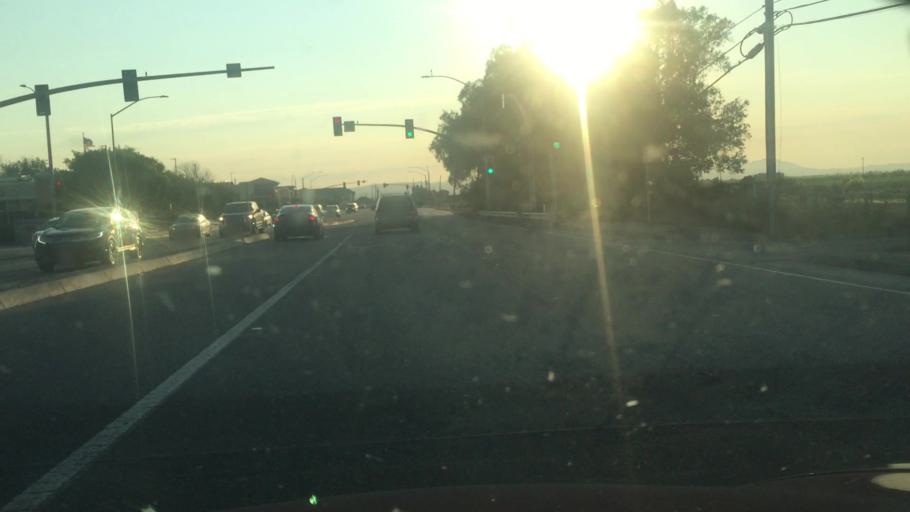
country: US
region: California
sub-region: San Joaquin County
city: Tracy
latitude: 37.7541
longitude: -121.4717
